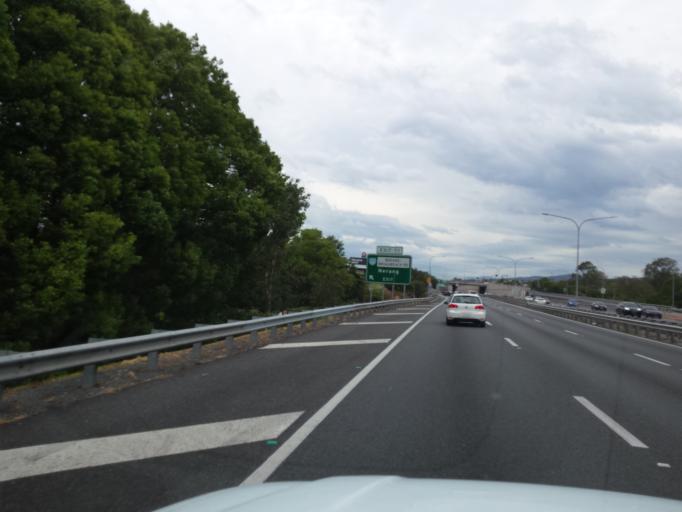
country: AU
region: Queensland
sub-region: Gold Coast
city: Nerang
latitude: -27.9899
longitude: 153.3407
